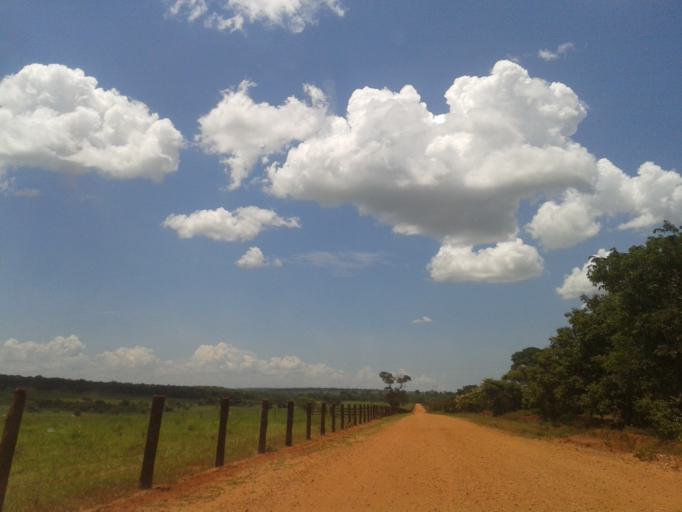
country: BR
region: Minas Gerais
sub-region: Santa Vitoria
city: Santa Vitoria
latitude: -19.2031
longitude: -50.3957
